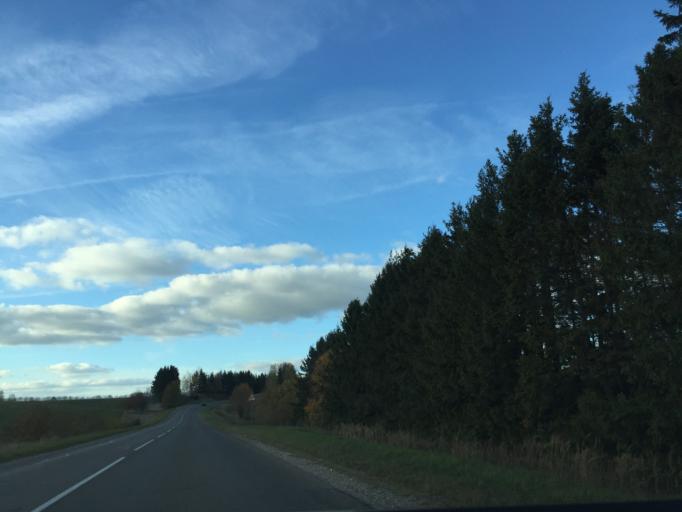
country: LV
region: Tukuma Rajons
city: Tukums
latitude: 56.9925
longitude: 23.0921
